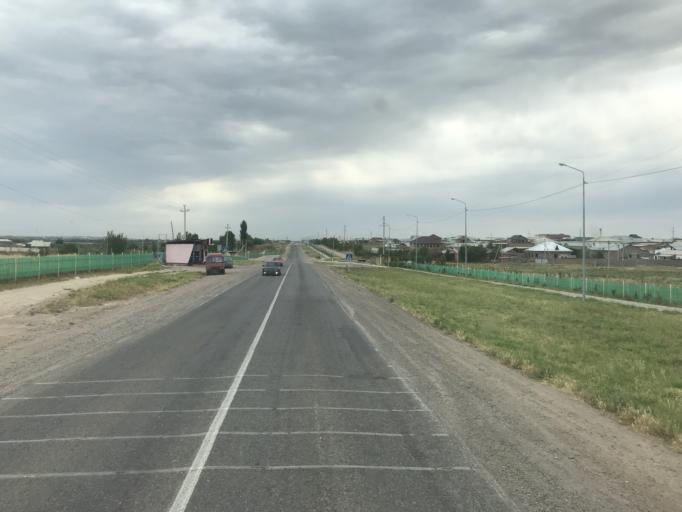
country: KZ
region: Ongtustik Qazaqstan
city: Saryaghash
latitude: 41.4218
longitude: 69.0913
